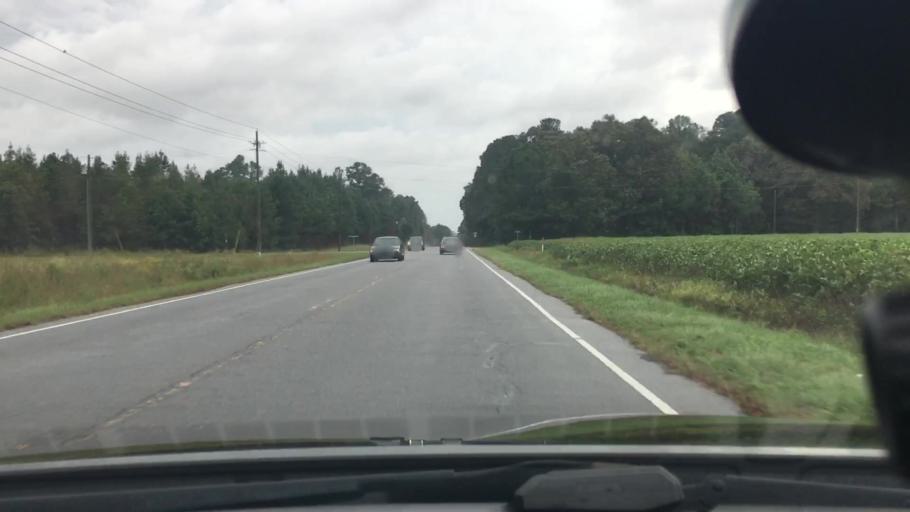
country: US
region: North Carolina
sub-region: Pitt County
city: Windsor
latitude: 35.4379
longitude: -77.2631
